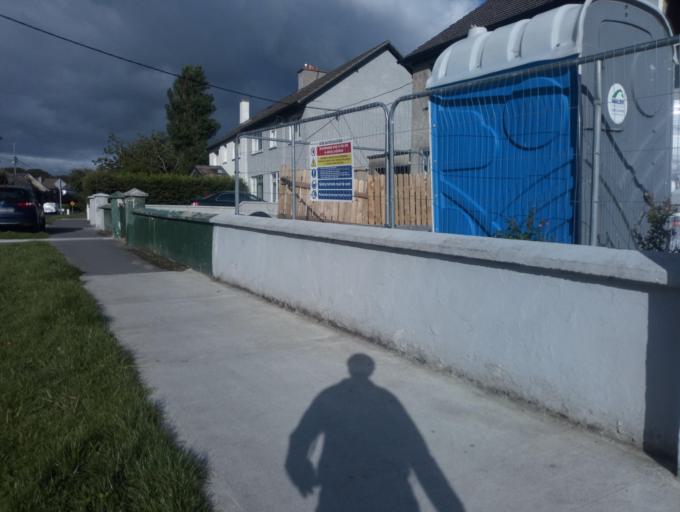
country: IE
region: Connaught
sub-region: County Galway
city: Gaillimh
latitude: 53.2654
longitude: -9.0755
